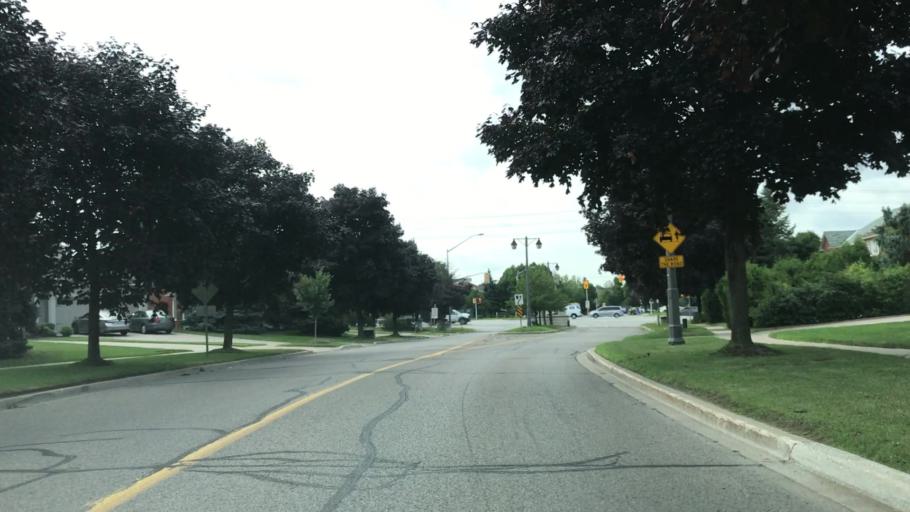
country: CA
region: Ontario
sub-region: York
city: Richmond Hill
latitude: 43.8599
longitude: -79.4034
